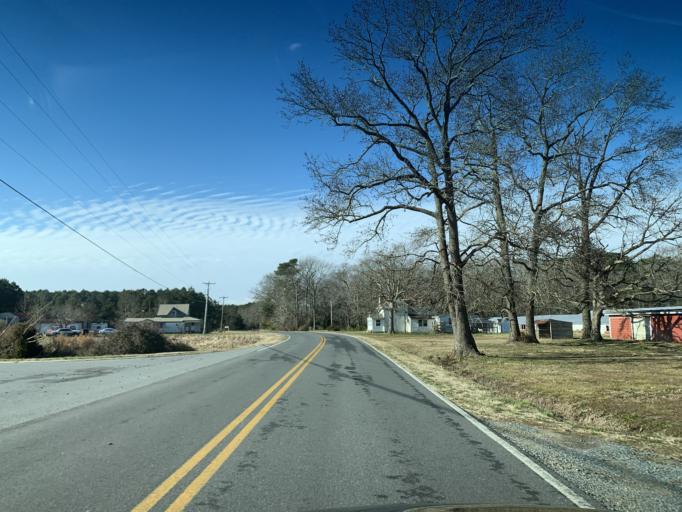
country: US
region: Maryland
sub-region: Worcester County
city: Ocean Pines
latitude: 38.4174
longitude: -75.1347
